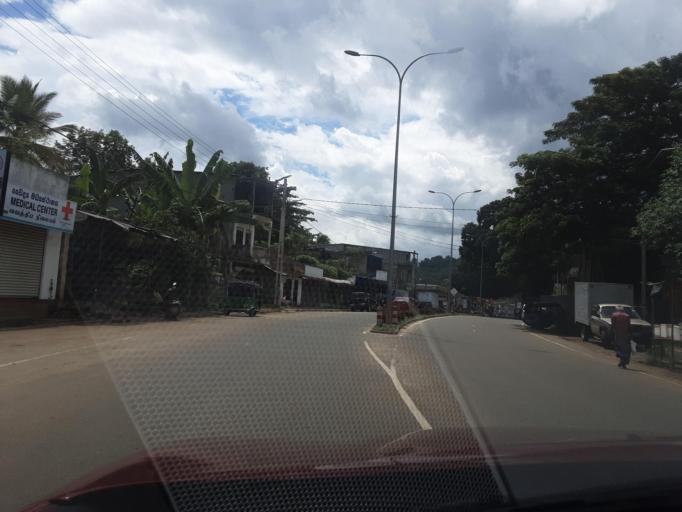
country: LK
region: Uva
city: Monaragala
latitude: 6.8958
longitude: 81.2381
